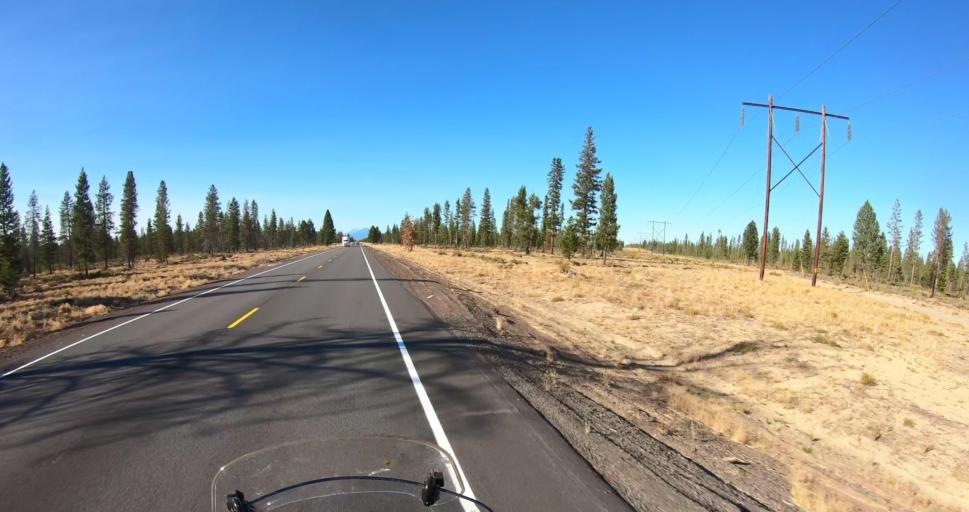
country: US
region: Oregon
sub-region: Deschutes County
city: La Pine
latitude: 43.5633
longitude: -121.4782
